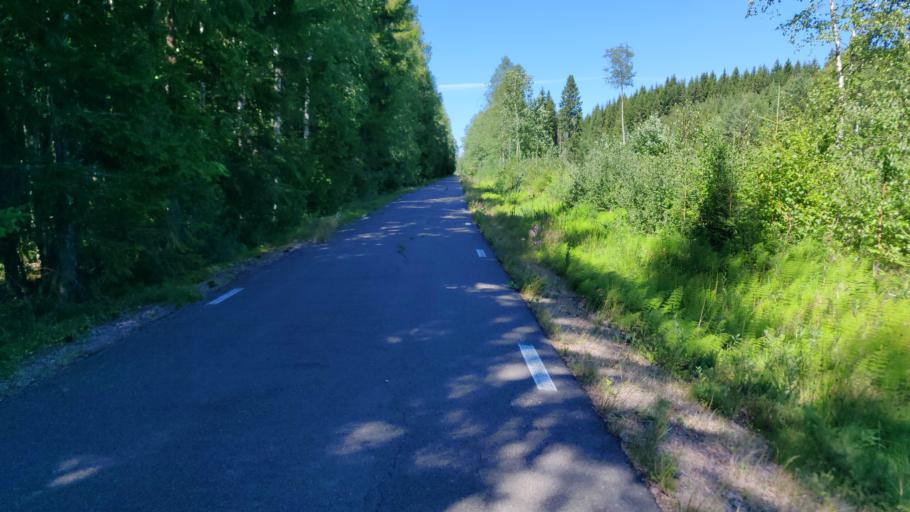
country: SE
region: Vaermland
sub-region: Hagfors Kommun
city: Hagfors
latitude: 59.9621
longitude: 13.5723
